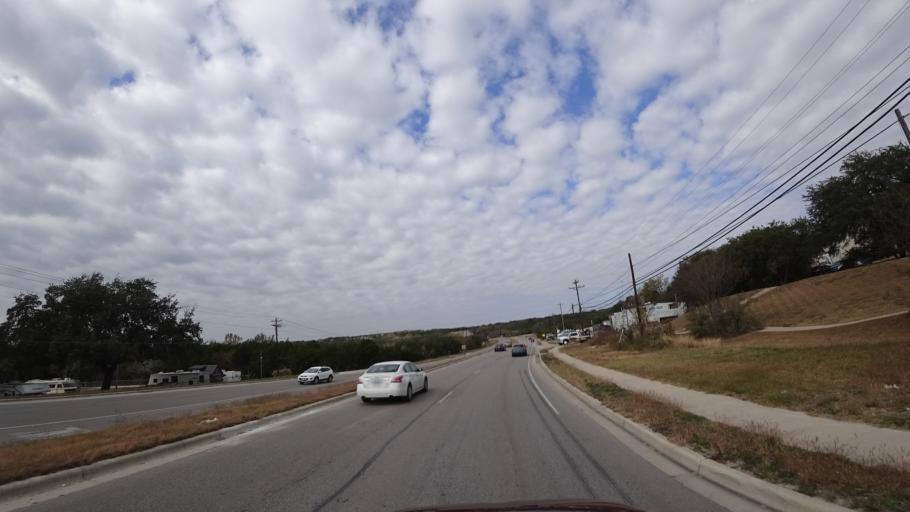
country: US
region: Texas
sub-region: Williamson County
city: Anderson Mill
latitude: 30.4577
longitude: -97.8344
